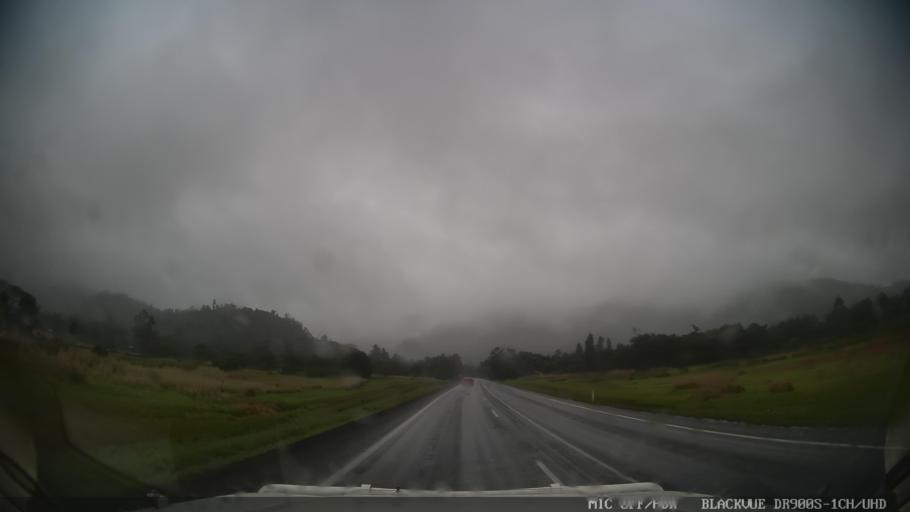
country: AU
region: Queensland
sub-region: Cassowary Coast
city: Innisfail
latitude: -17.8656
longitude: 145.9819
